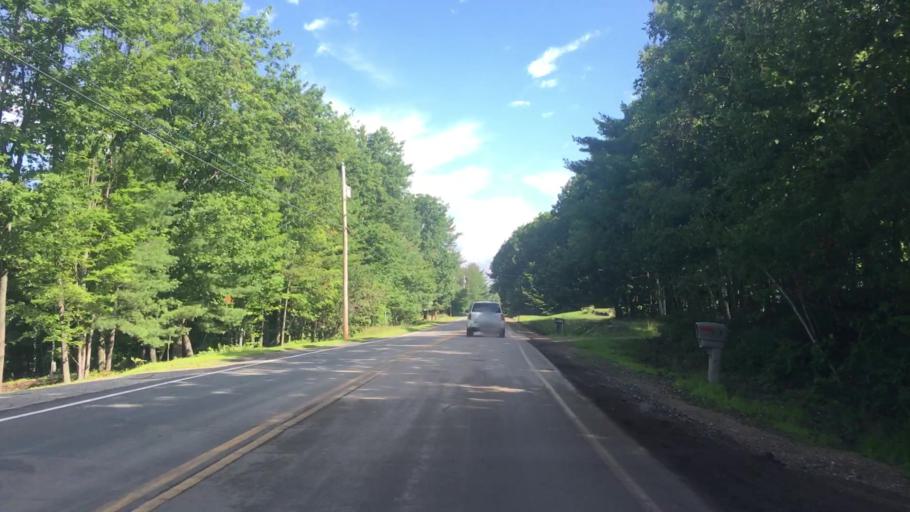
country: US
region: New Hampshire
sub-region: Belknap County
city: Gilford
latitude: 43.5310
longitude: -71.3461
